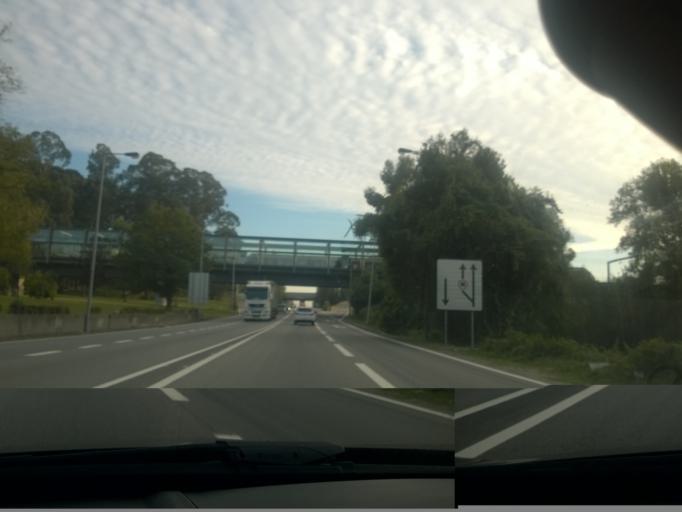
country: PT
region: Porto
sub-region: Maia
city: Maia
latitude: 41.2299
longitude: -8.6267
